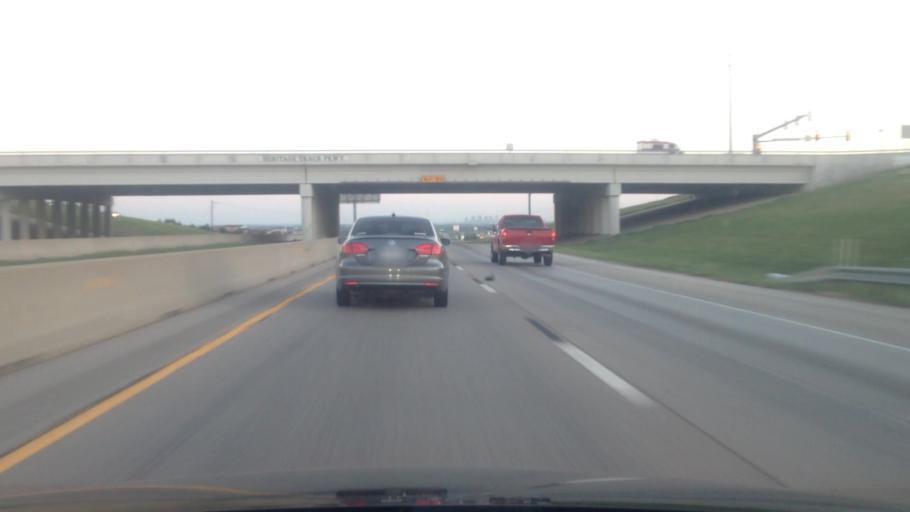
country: US
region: Texas
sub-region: Tarrant County
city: Blue Mound
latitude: 32.9156
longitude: -97.3173
